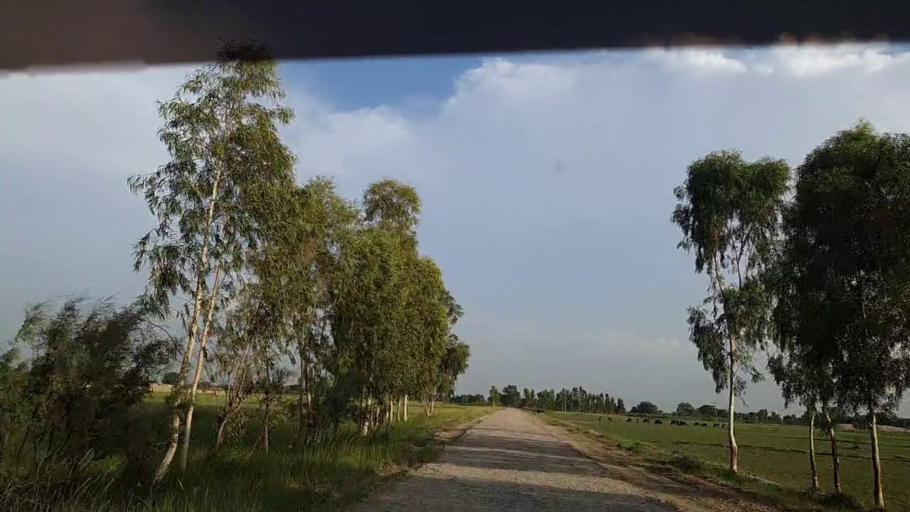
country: PK
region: Sindh
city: Khanpur
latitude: 27.8129
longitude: 69.3367
